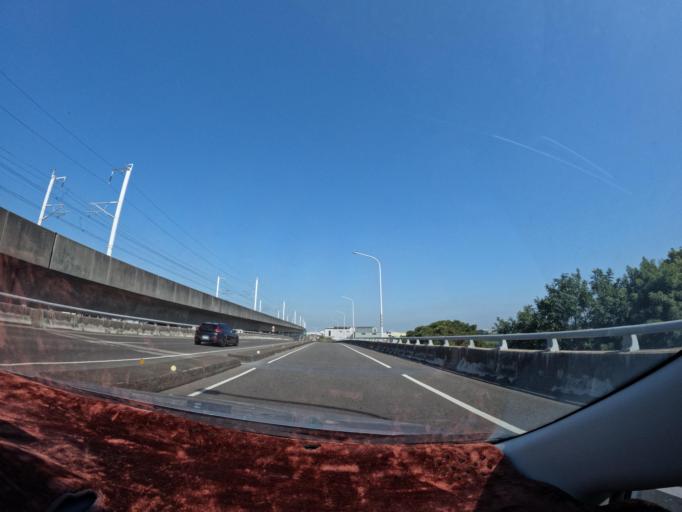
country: TW
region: Taiwan
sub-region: Tainan
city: Tainan
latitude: 23.0174
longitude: 120.2891
